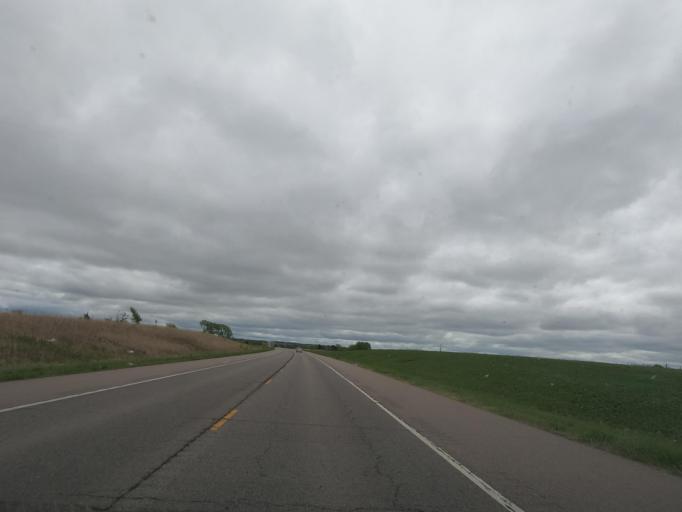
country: US
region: Kansas
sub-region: Elk County
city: Howard
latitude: 37.6366
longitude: -96.3847
